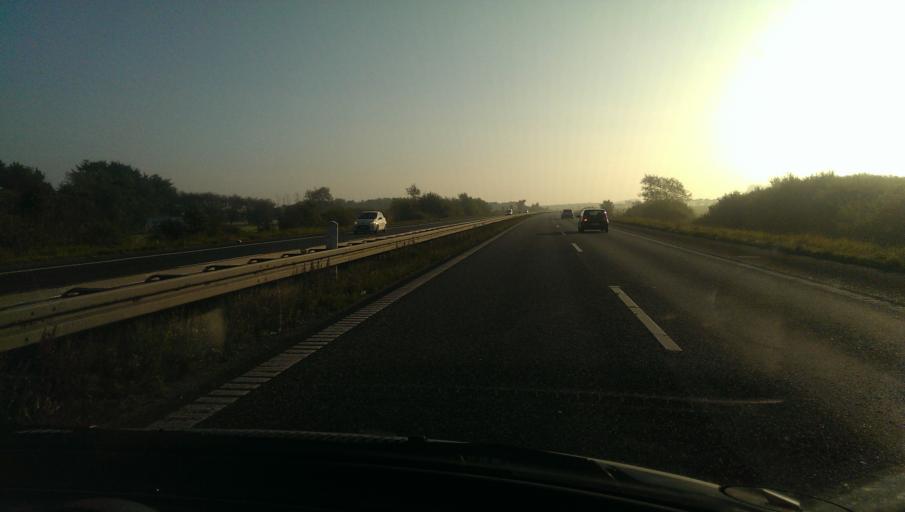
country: DK
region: South Denmark
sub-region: Vejen Kommune
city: Vejen
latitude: 55.4941
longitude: 9.1897
